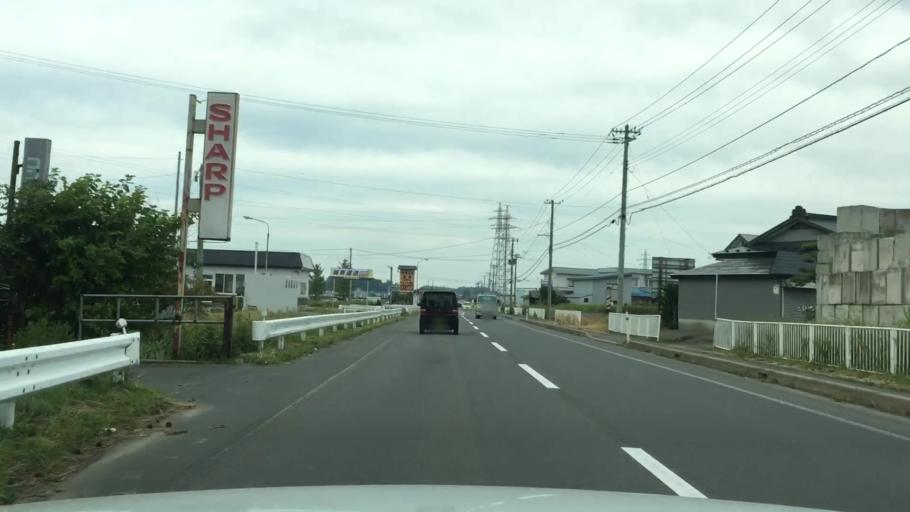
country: JP
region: Aomori
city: Hirosaki
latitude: 40.6318
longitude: 140.4517
